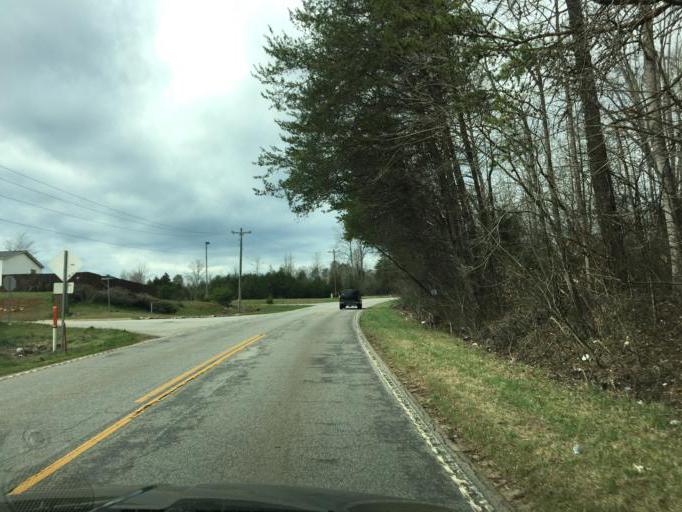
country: US
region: South Carolina
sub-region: Anderson County
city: Piedmont
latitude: 34.7002
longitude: -82.4277
